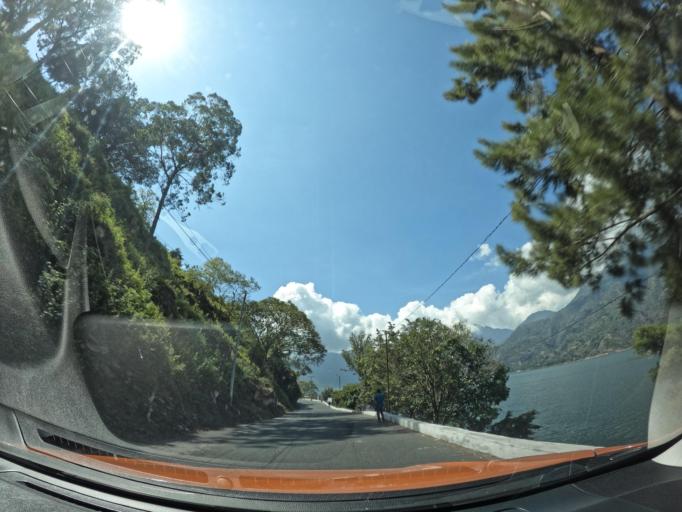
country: GT
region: Solola
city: Santiago Atitlan
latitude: 14.6331
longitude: -91.2312
